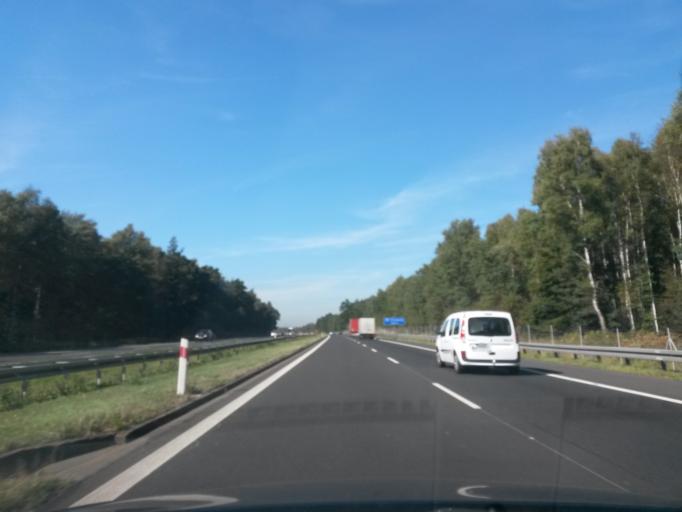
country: PL
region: Lesser Poland Voivodeship
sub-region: Powiat chrzanowski
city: Bolecin
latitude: 50.1318
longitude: 19.4778
